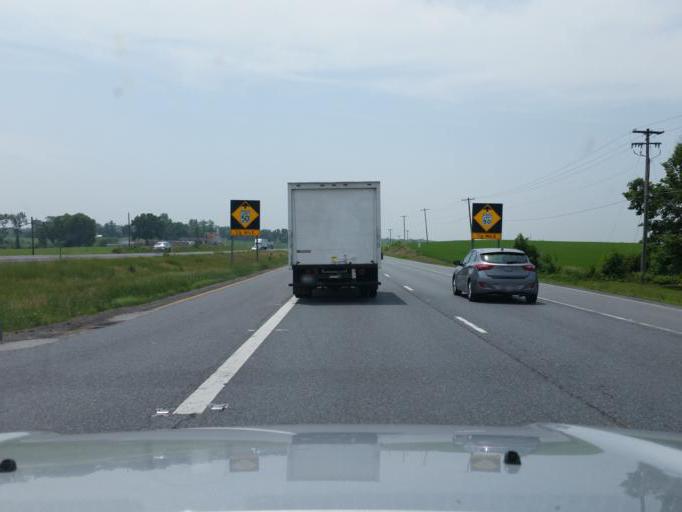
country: US
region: Maryland
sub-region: Frederick County
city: Clover Hill
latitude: 39.4862
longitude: -77.3976
